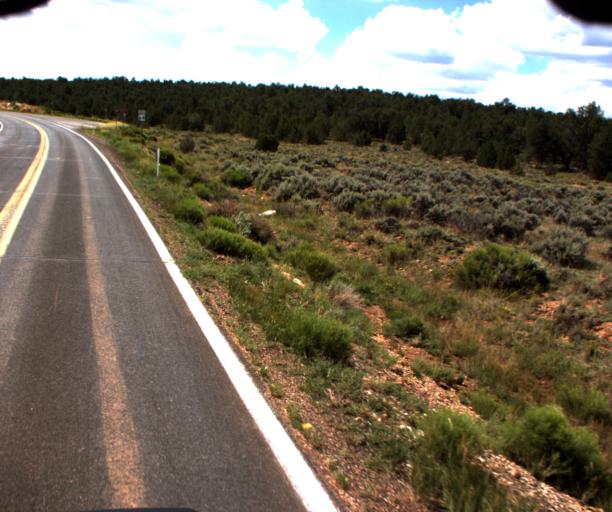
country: US
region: Arizona
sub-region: Coconino County
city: Grand Canyon
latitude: 36.0062
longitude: -111.8032
